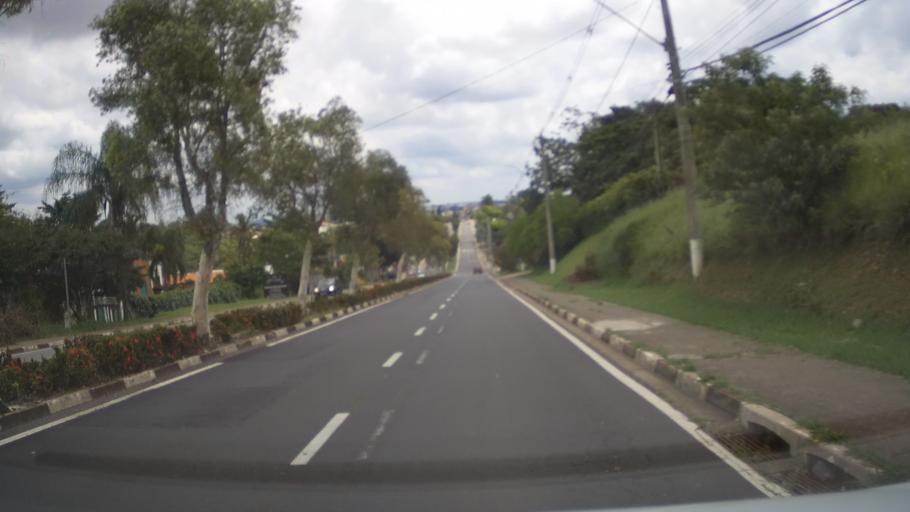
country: BR
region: Sao Paulo
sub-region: Vinhedo
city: Vinhedo
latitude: -23.0258
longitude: -46.9619
